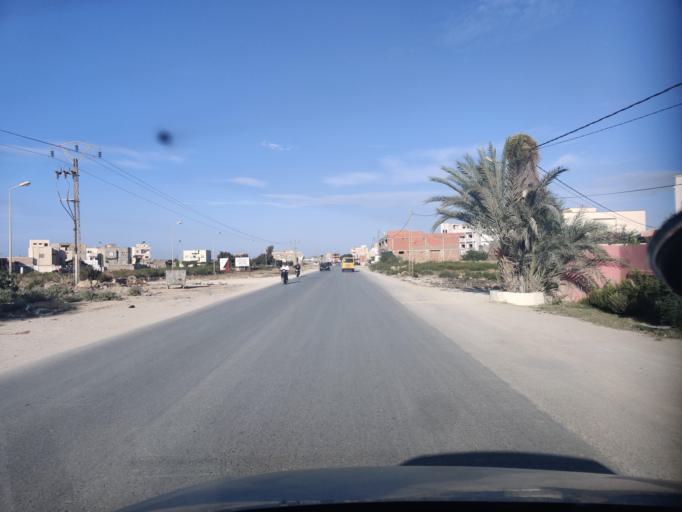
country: TN
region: Ariana
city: Ariana
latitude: 36.9566
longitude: 10.2098
